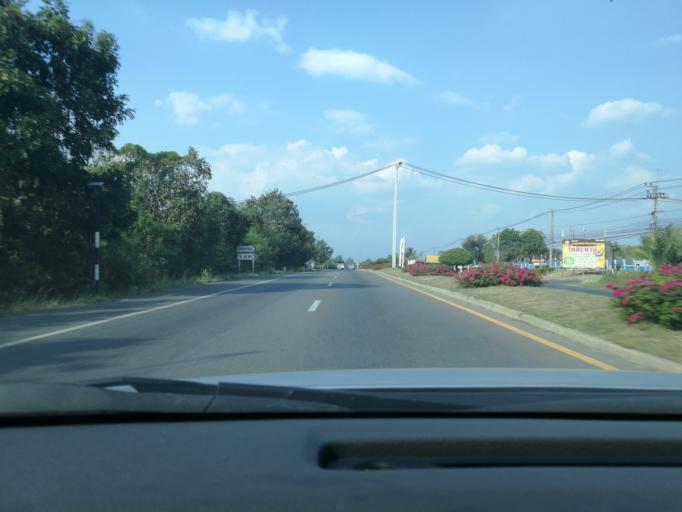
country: TH
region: Phetchabun
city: Phetchabun
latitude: 16.2181
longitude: 101.0890
